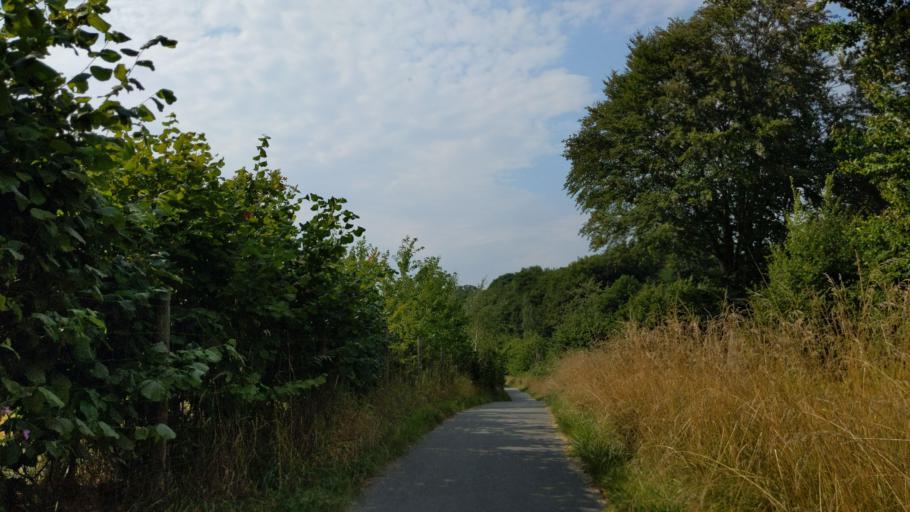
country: DE
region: Schleswig-Holstein
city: Behlendorf
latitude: 53.7017
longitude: 10.6622
